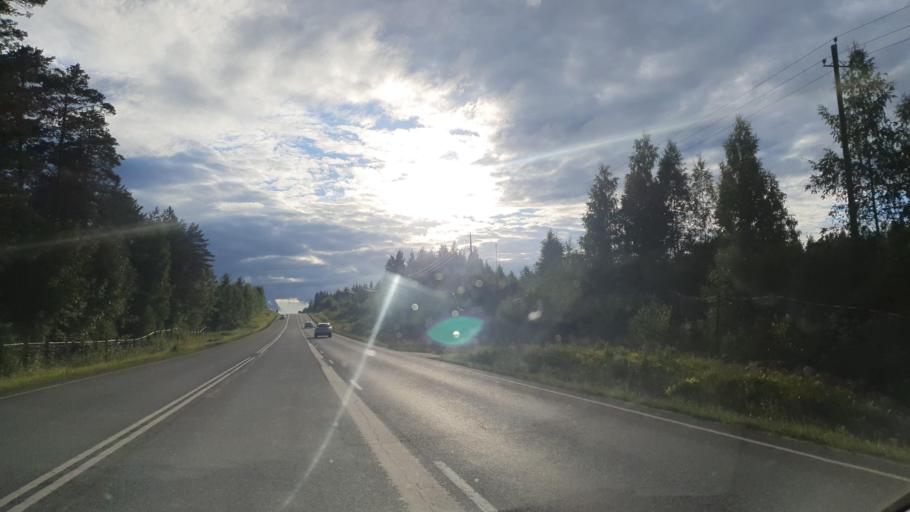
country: FI
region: Southern Savonia
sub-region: Mikkeli
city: Pertunmaa
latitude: 61.4358
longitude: 26.5458
